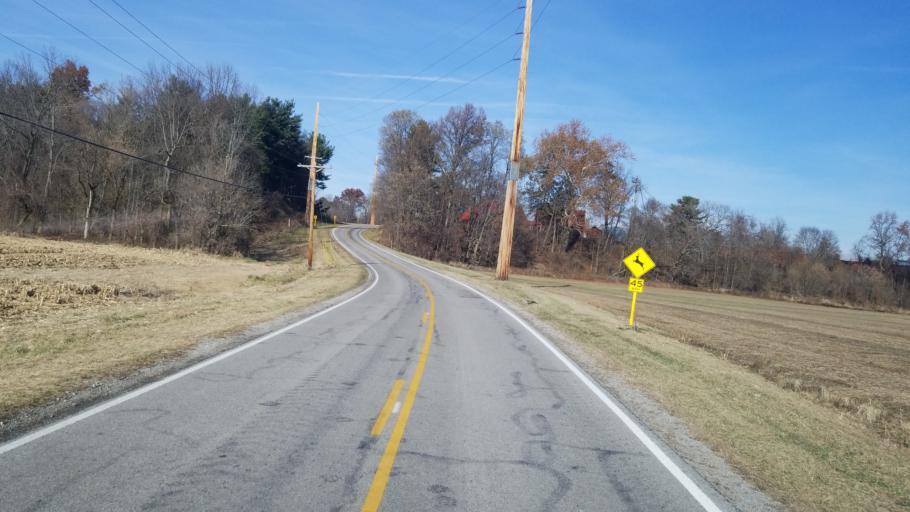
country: US
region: Ohio
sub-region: Huron County
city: Willard
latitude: 41.1271
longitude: -82.6863
